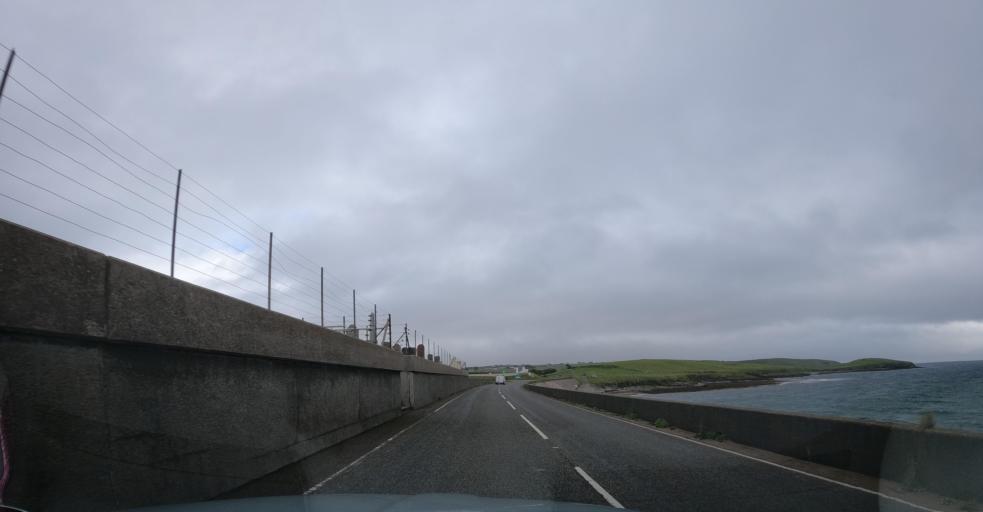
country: GB
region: Scotland
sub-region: Eilean Siar
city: Stornoway
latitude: 58.2055
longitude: -6.2881
